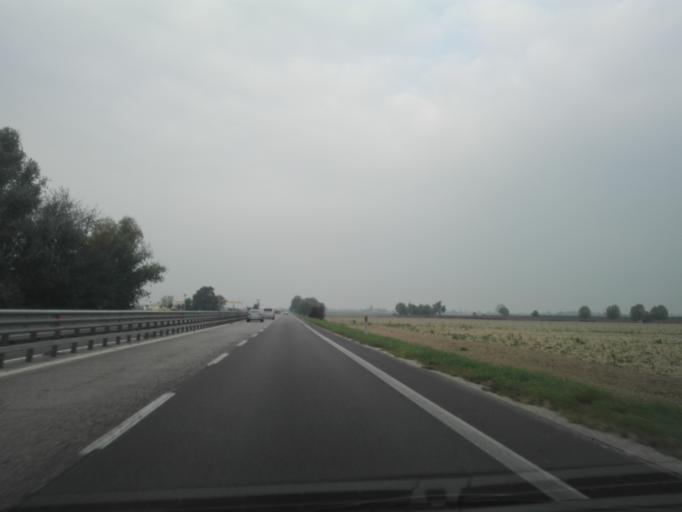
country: IT
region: Veneto
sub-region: Provincia di Verona
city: Villa Bartolomea
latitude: 45.1512
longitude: 11.3376
